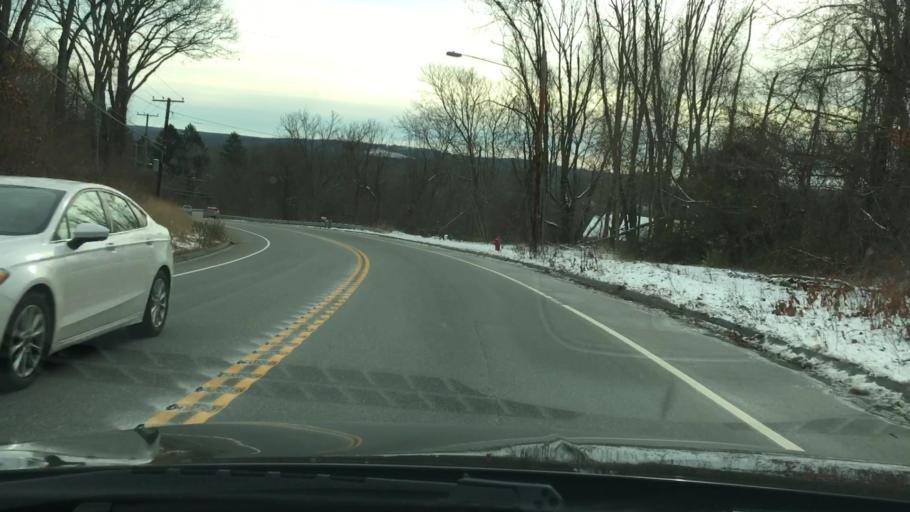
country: US
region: Connecticut
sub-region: New London County
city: Norwich
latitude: 41.4954
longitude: -72.0762
